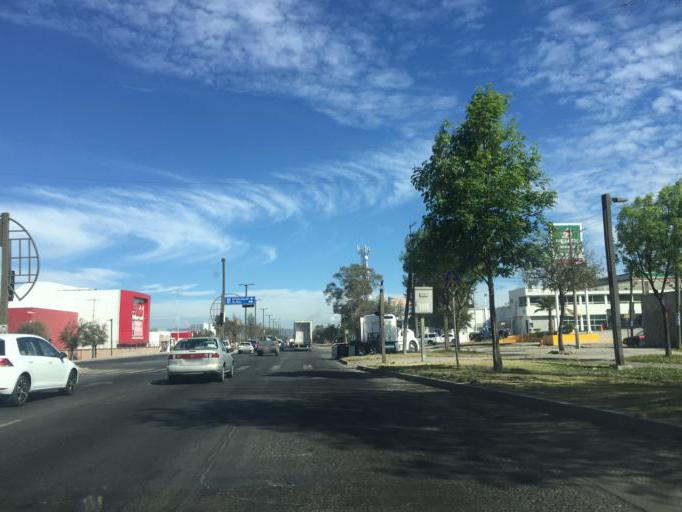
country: MX
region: Queretaro
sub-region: San Juan del Rio
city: Santa Cruz Escandon
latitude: 20.4106
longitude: -99.9815
